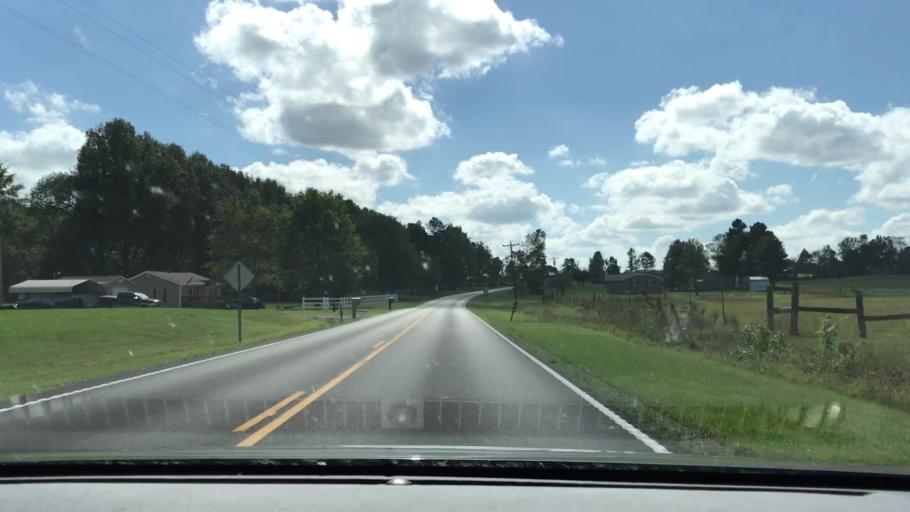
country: US
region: Kentucky
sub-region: Graves County
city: Mayfield
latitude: 36.8584
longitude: -88.5717
